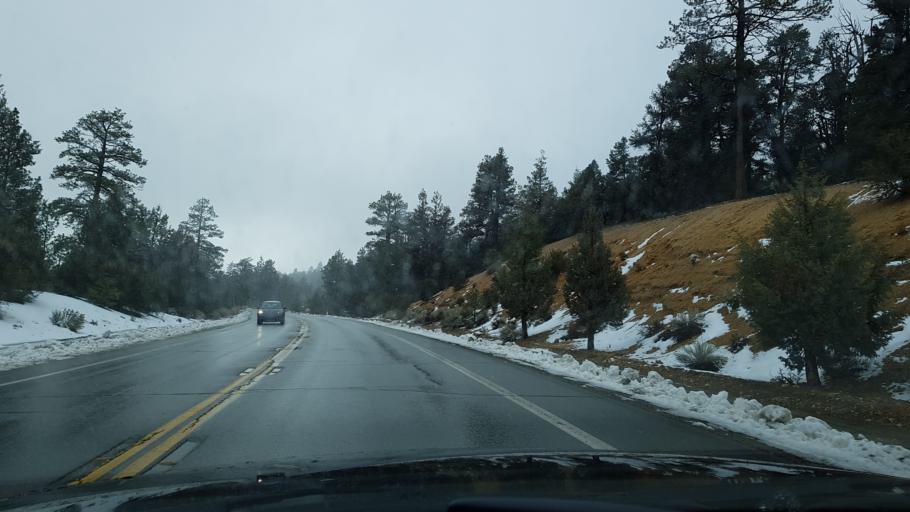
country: US
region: California
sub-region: San Bernardino County
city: Big Bear Lake
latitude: 34.2643
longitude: -116.9142
